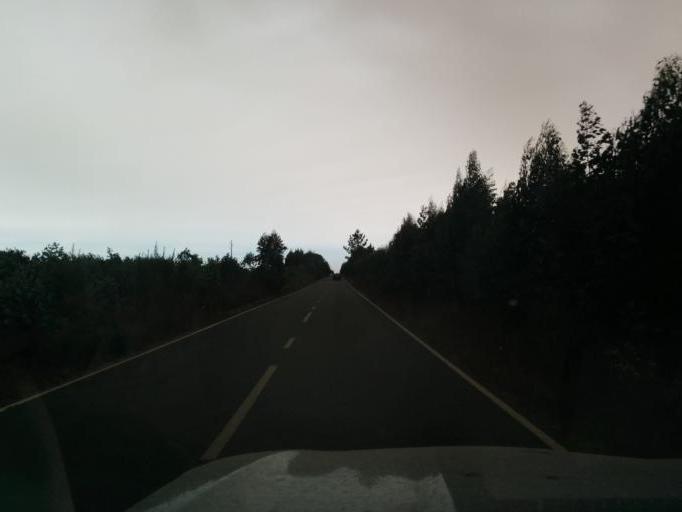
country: PT
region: Beja
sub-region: Odemira
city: Sao Teotonio
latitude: 37.5773
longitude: -8.7380
